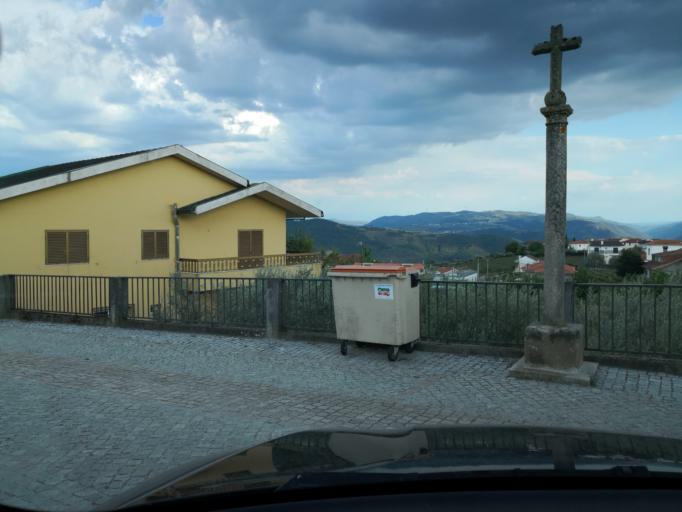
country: PT
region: Vila Real
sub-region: Sabrosa
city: Vilela
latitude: 41.2083
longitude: -7.6596
